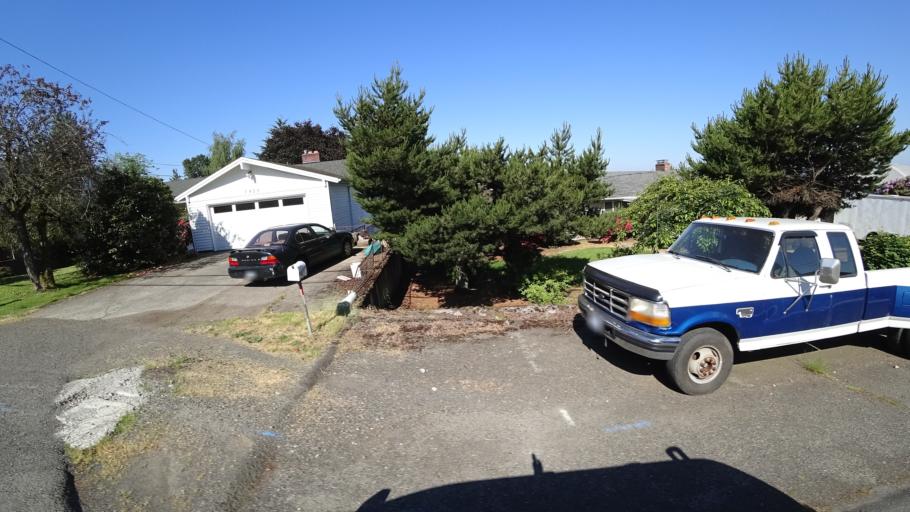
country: US
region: Oregon
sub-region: Multnomah County
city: Lents
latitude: 45.4659
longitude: -122.5481
